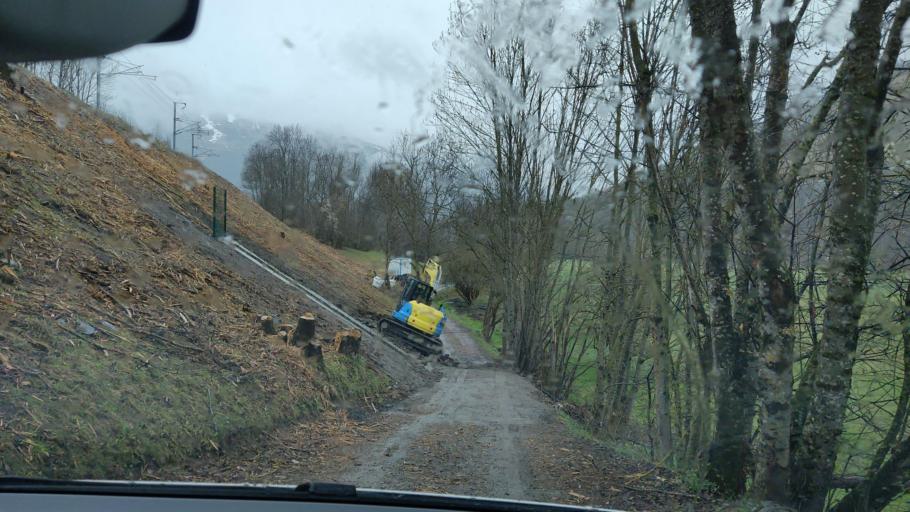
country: FR
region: Rhone-Alpes
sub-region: Departement de la Savoie
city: Bourg-Saint-Maurice
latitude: 45.5922
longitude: 6.7549
